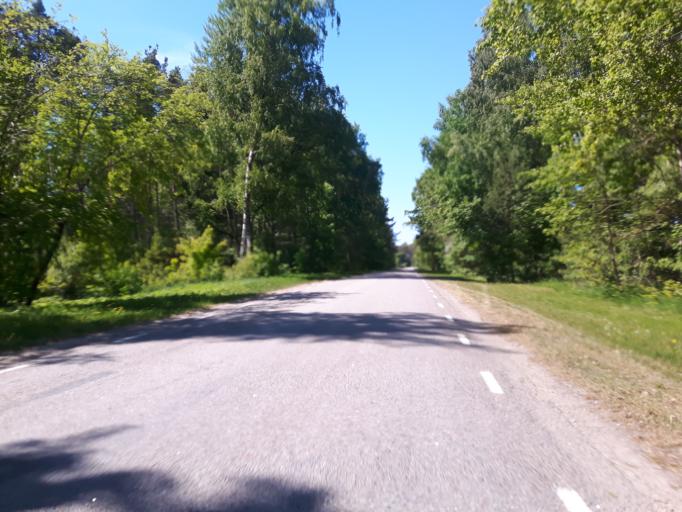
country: EE
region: Laeaene-Virumaa
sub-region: Viru-Nigula vald
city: Kunda
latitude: 59.4945
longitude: 26.4998
